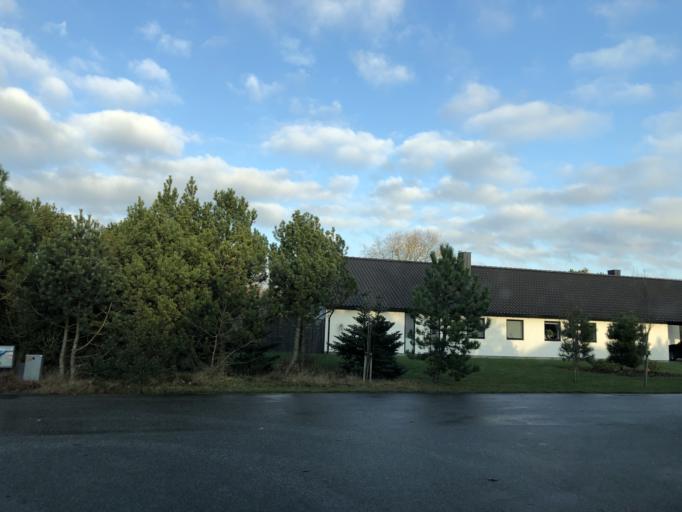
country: DK
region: Central Jutland
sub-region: Holstebro Kommune
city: Ulfborg
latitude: 56.3204
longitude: 8.4353
